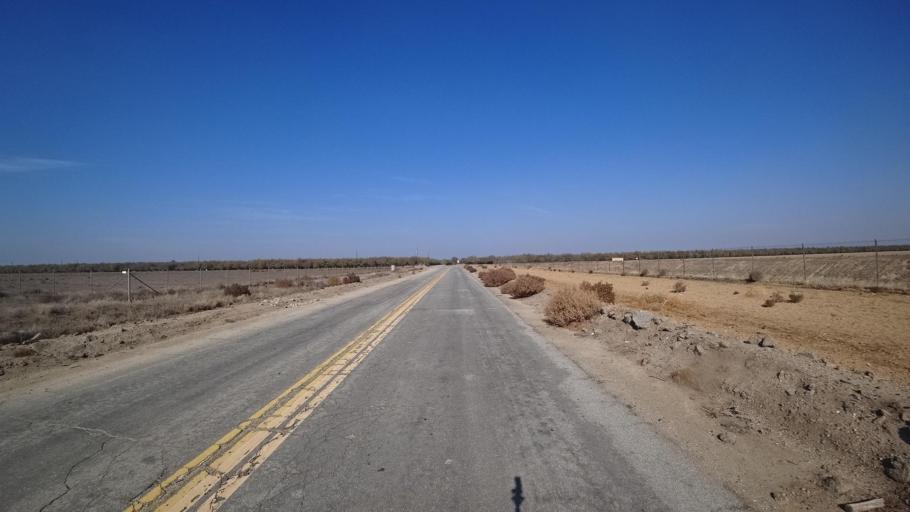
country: US
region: California
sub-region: Kern County
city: Shafter
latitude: 35.5348
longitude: -119.1868
